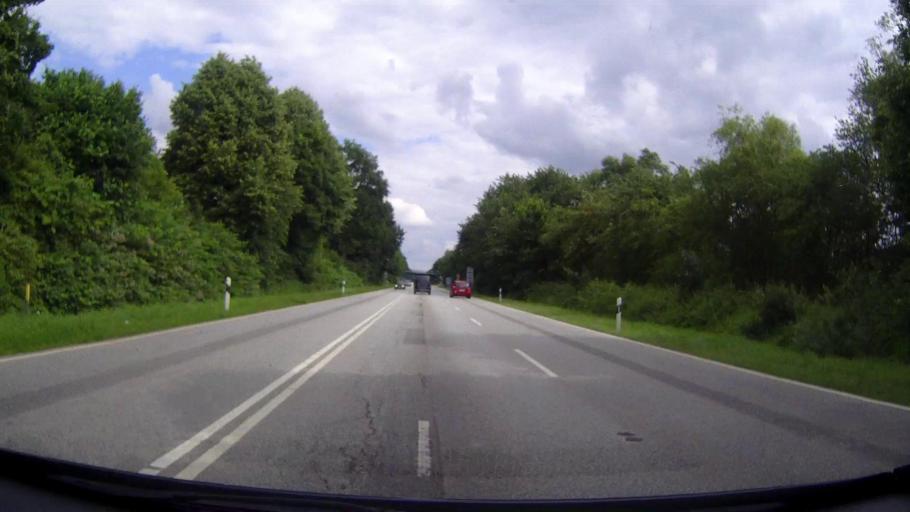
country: DE
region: Schleswig-Holstein
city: Klein Gladebrugge
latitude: 53.9301
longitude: 10.3157
